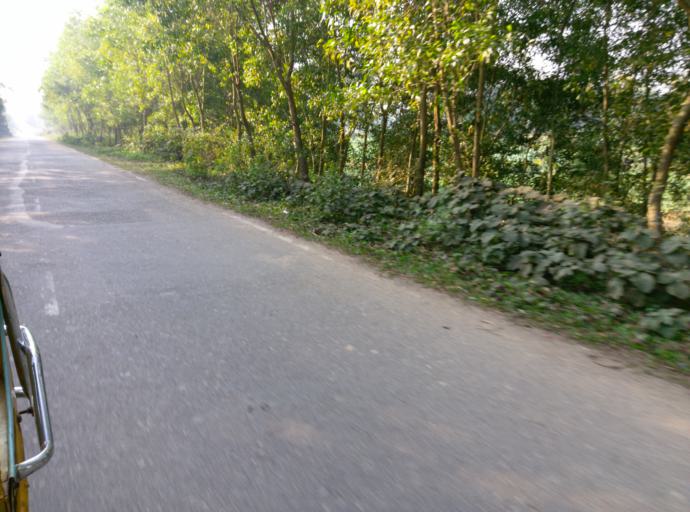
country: BD
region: Dhaka
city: Netrakona
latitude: 25.1371
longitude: 90.6615
